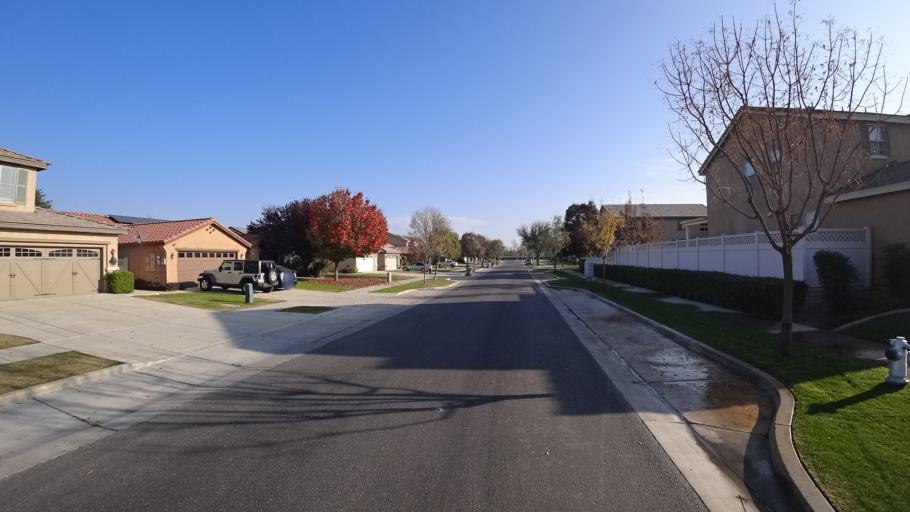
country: US
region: California
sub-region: Kern County
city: Rosedale
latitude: 35.3595
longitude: -119.1426
